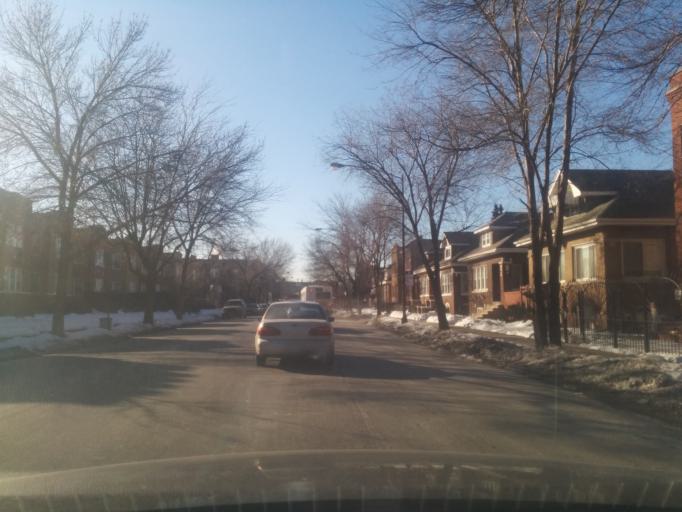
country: US
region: Illinois
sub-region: Cook County
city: Oak Park
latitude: 41.9110
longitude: -87.7753
